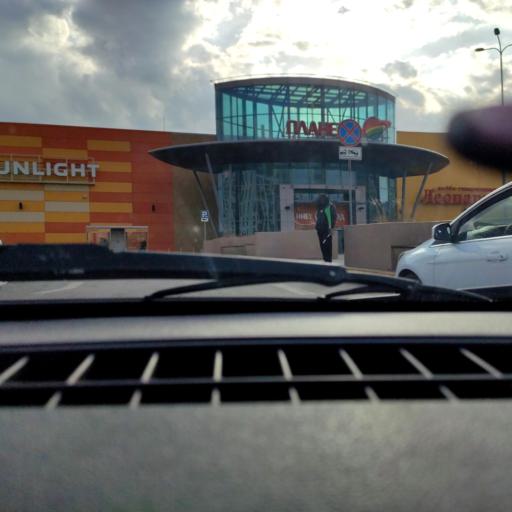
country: RU
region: Bashkortostan
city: Ufa
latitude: 54.7579
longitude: 56.0339
